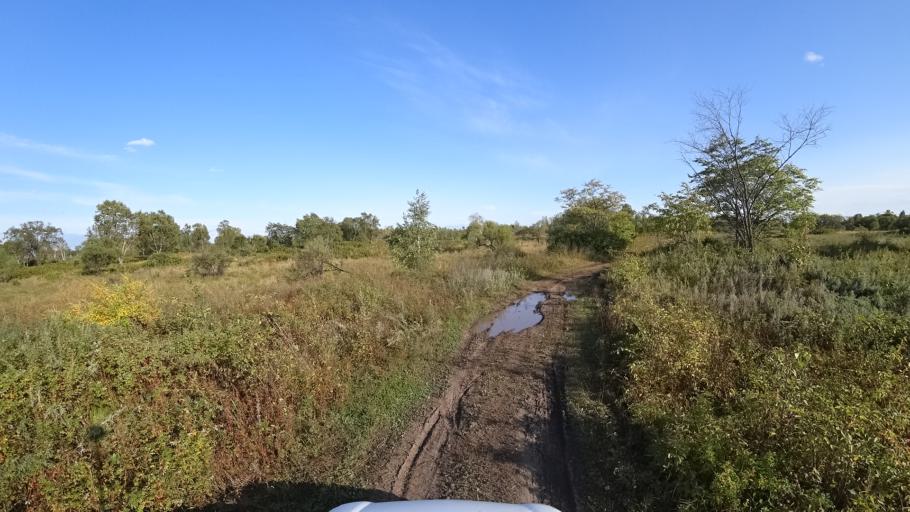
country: RU
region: Amur
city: Arkhara
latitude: 49.3494
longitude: 130.1232
